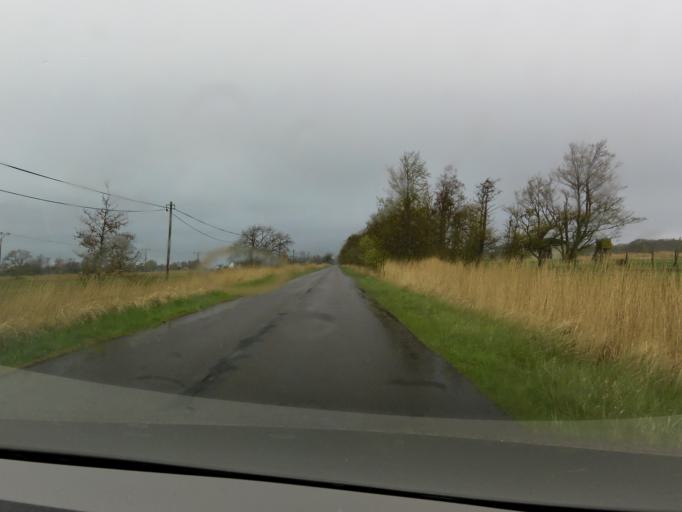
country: DE
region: Mecklenburg-Vorpommern
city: Zingst
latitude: 54.4217
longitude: 12.7447
